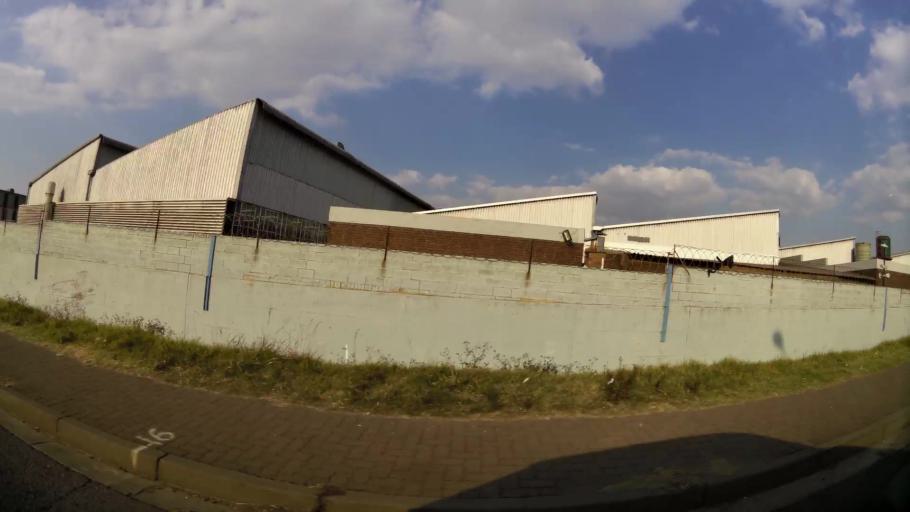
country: ZA
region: Gauteng
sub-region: City of Johannesburg Metropolitan Municipality
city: Modderfontein
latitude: -26.1174
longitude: 28.2081
